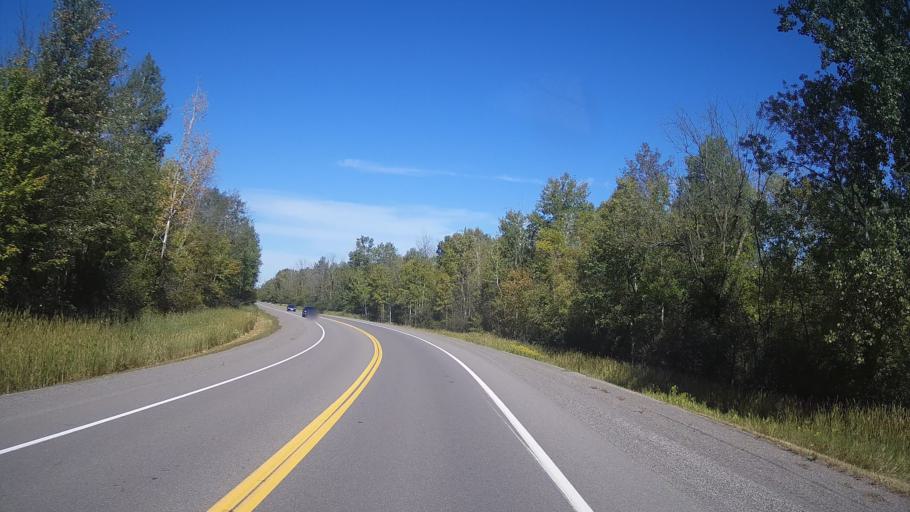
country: CA
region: Ontario
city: Bells Corners
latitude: 45.0774
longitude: -75.6487
